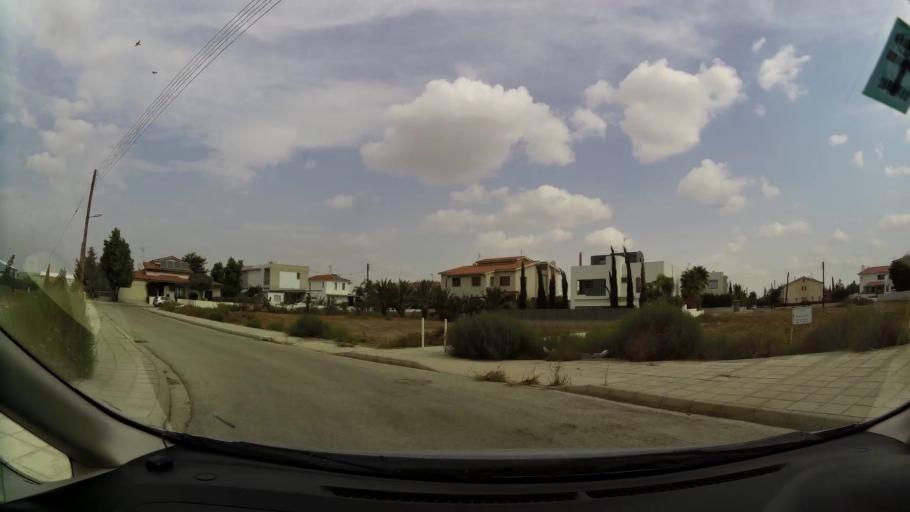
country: CY
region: Lefkosia
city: Geri
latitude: 35.0816
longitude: 33.3871
